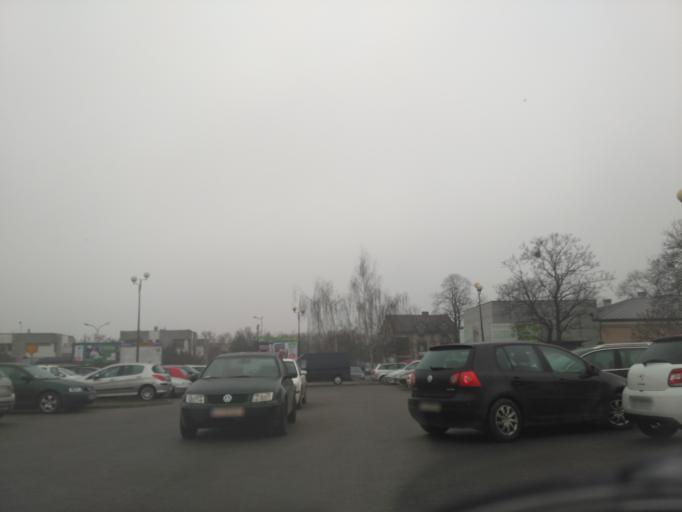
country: PL
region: Lublin Voivodeship
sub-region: Chelm
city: Chelm
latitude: 51.1306
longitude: 23.4736
